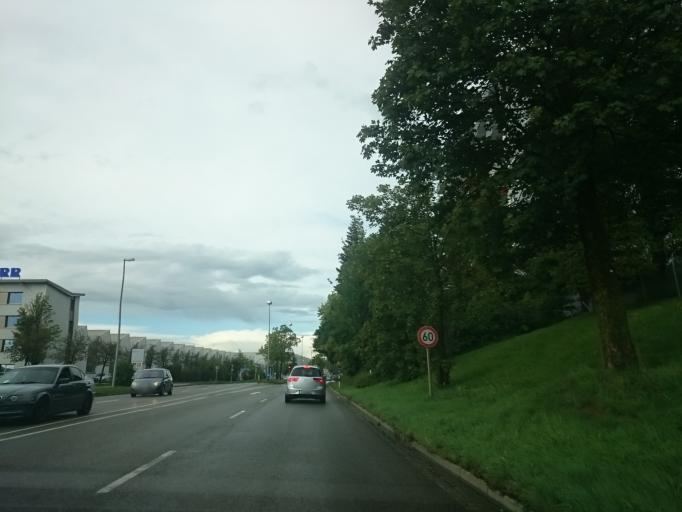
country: DE
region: Bavaria
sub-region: Swabia
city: Kempten (Allgaeu)
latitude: 47.7421
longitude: 10.3231
